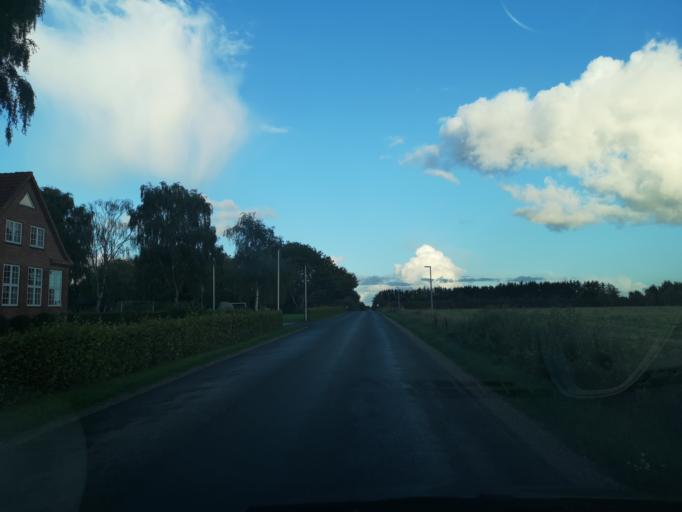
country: DK
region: Central Jutland
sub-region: Ringkobing-Skjern Kommune
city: Skjern
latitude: 56.0229
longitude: 8.5487
